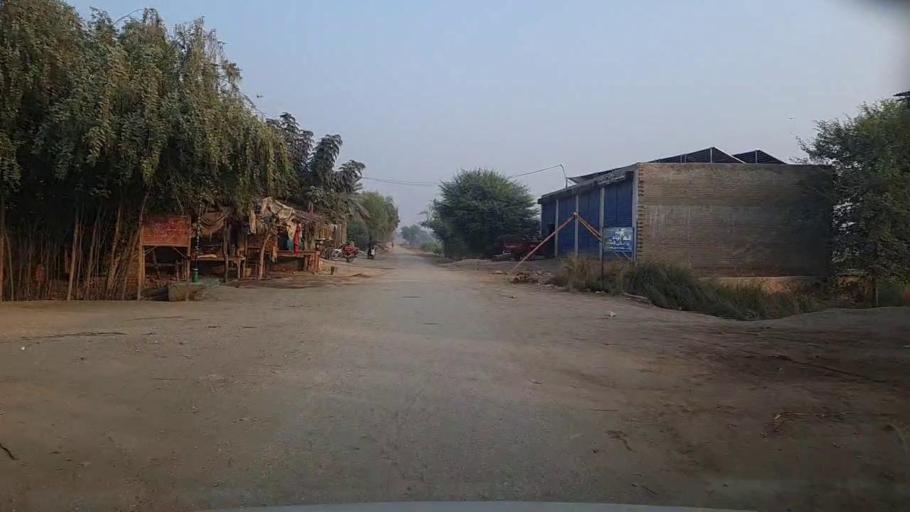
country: PK
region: Sindh
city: Bozdar
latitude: 27.0790
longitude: 68.5775
